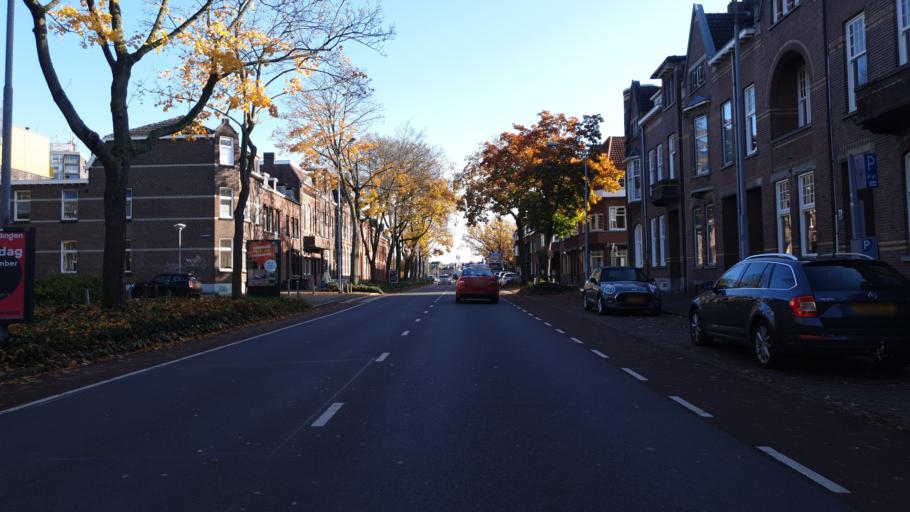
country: NL
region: Limburg
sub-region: Gemeente Venlo
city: Venlo
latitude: 51.3716
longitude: 6.1746
